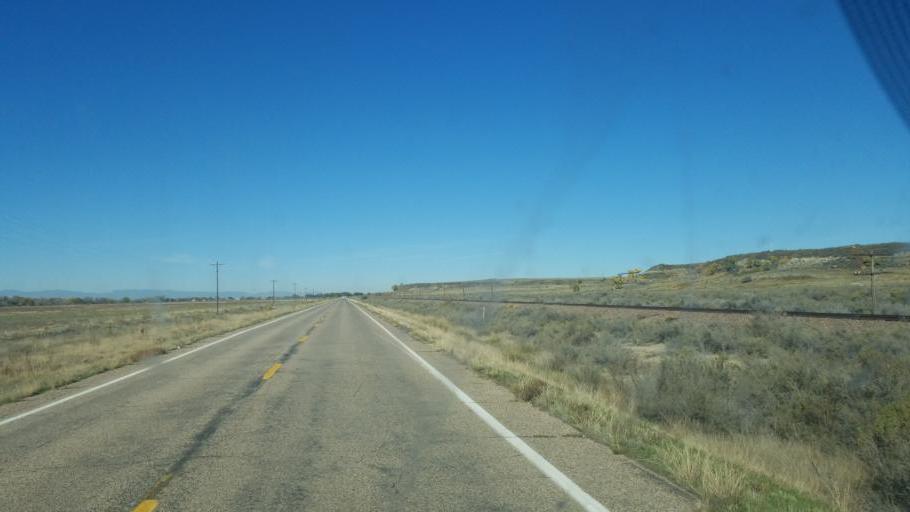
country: US
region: Colorado
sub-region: Pueblo County
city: Pueblo
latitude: 38.2558
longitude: -104.3126
